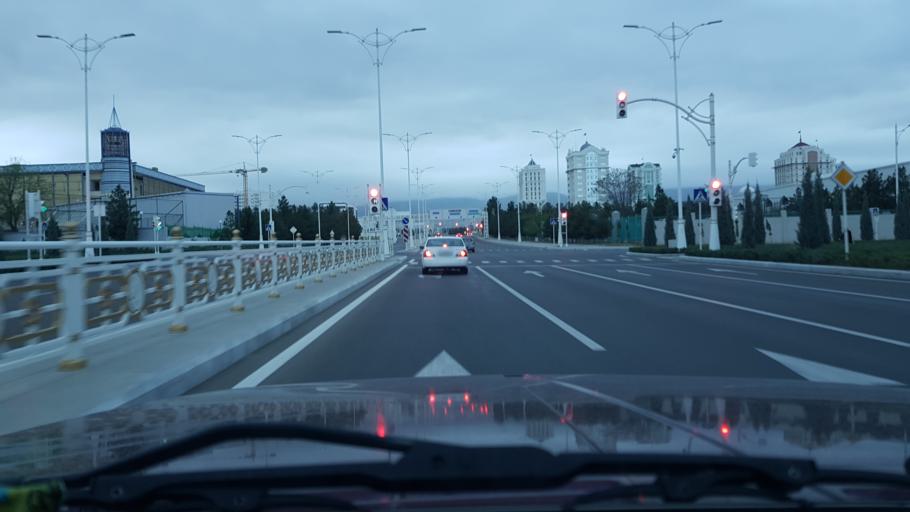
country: TM
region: Ahal
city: Ashgabat
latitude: 37.8866
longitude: 58.3610
